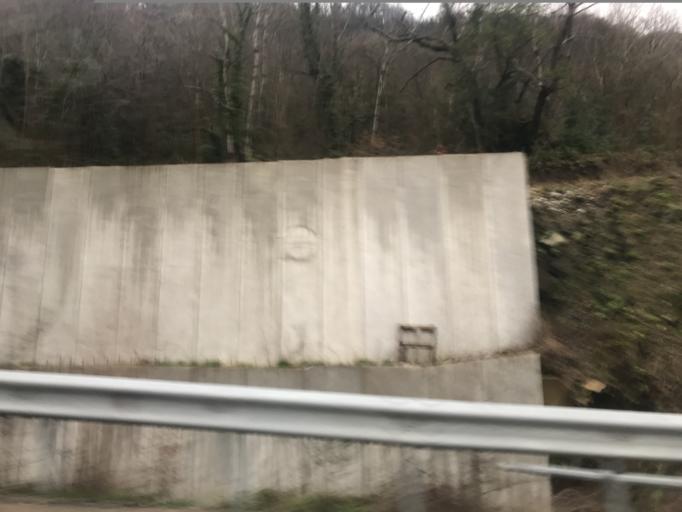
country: TR
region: Bartin
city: Amasra
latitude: 41.7281
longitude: 32.3845
